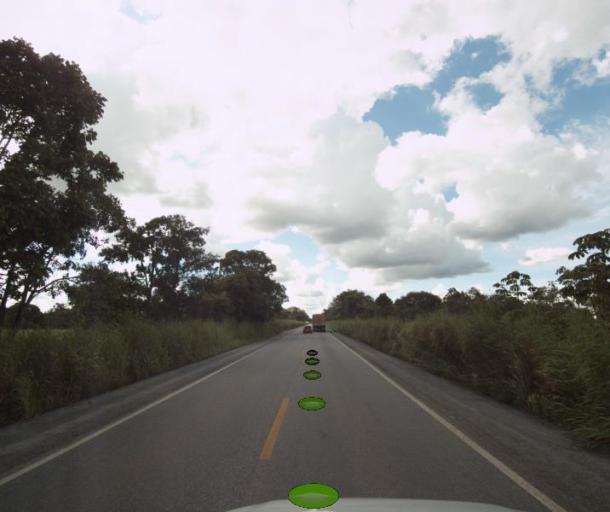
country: BR
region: Goias
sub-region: Porangatu
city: Porangatu
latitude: -13.1934
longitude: -49.1614
